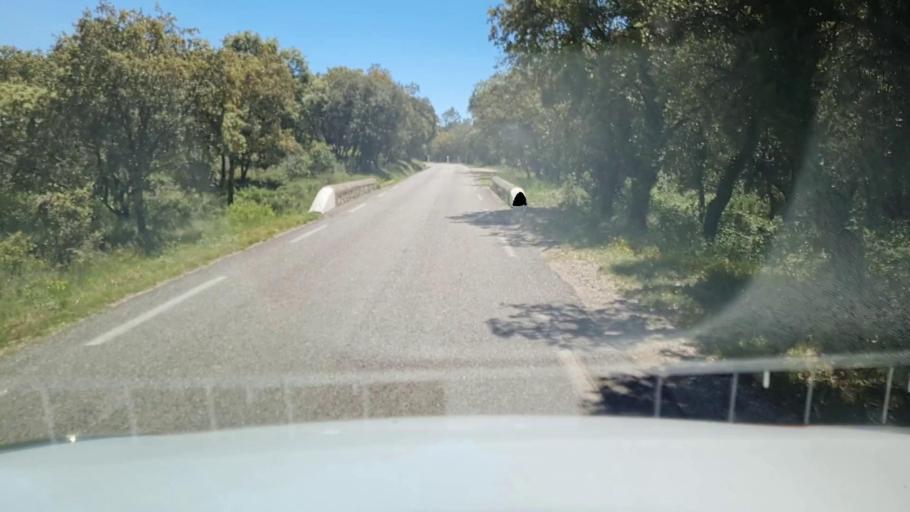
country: FR
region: Languedoc-Roussillon
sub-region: Departement du Gard
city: Clarensac
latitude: 43.8517
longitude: 4.2171
